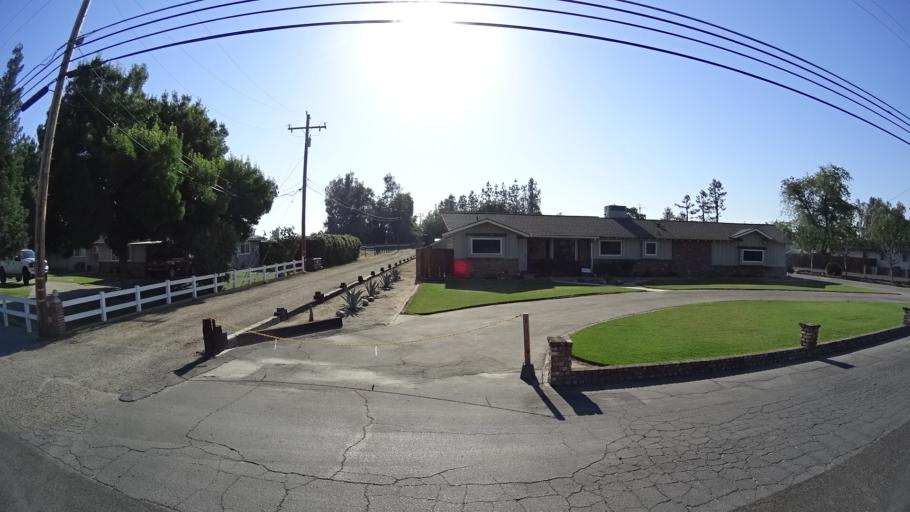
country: US
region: California
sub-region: Kings County
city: Armona
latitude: 36.3462
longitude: -119.7089
